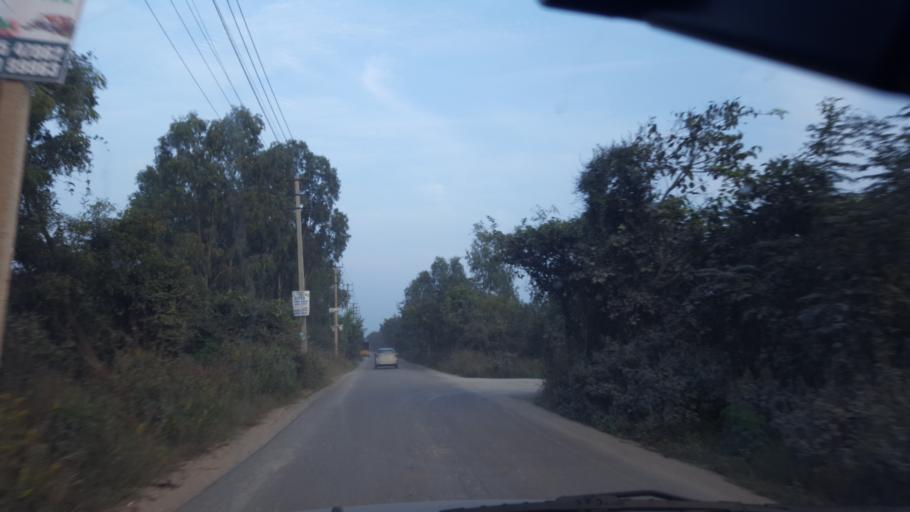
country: IN
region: Karnataka
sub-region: Bangalore Rural
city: Hoskote
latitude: 13.0767
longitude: 77.7009
